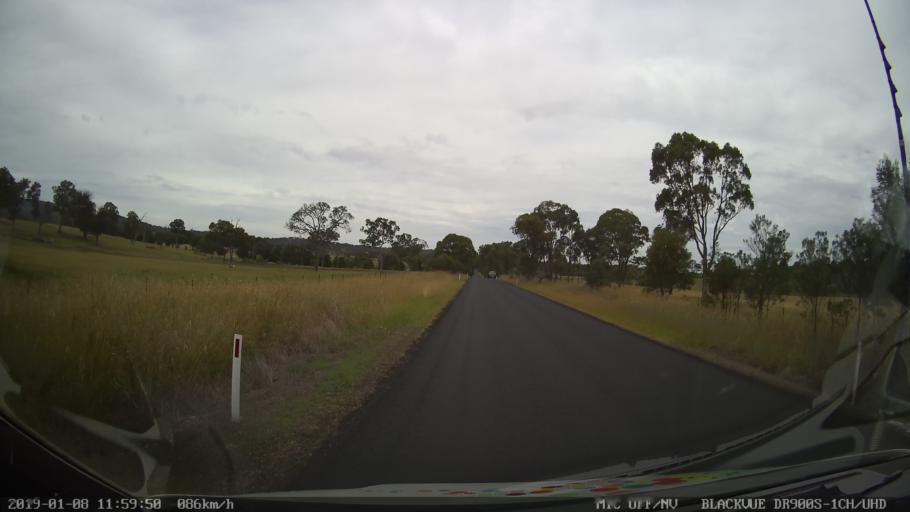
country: AU
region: New South Wales
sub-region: Armidale Dumaresq
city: Armidale
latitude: -30.4593
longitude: 151.5933
